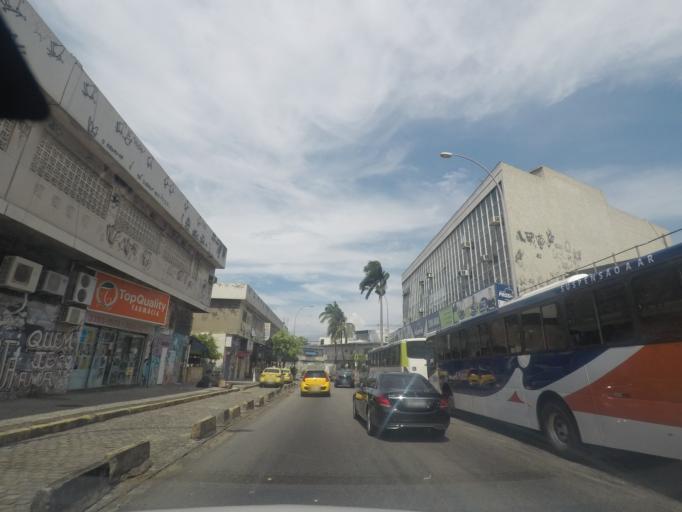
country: BR
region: Rio de Janeiro
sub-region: Rio De Janeiro
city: Rio de Janeiro
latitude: -22.8050
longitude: -43.2070
